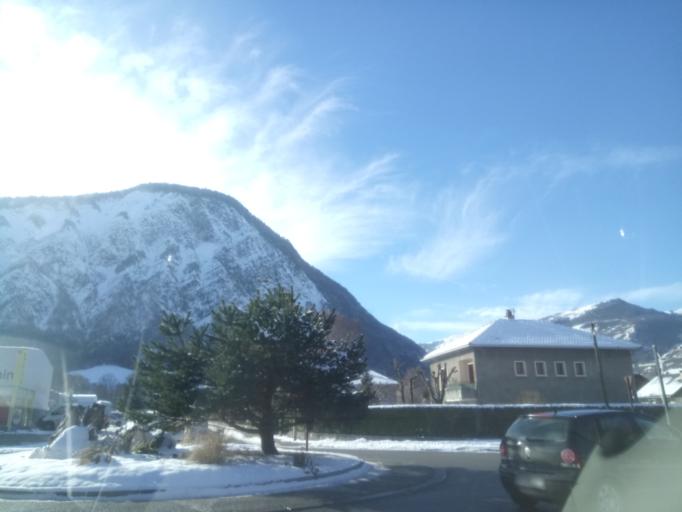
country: FR
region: Rhone-Alpes
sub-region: Departement de la Savoie
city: Villargondran
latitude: 45.2726
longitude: 6.3616
